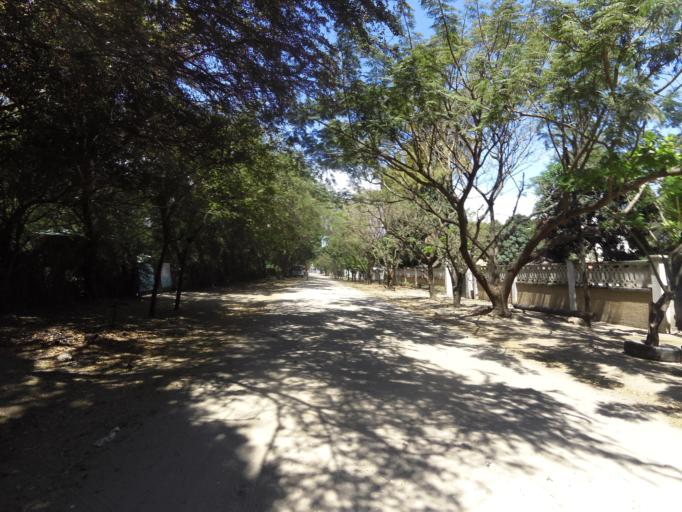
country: TZ
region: Dar es Salaam
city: Magomeni
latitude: -6.7941
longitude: 39.2716
